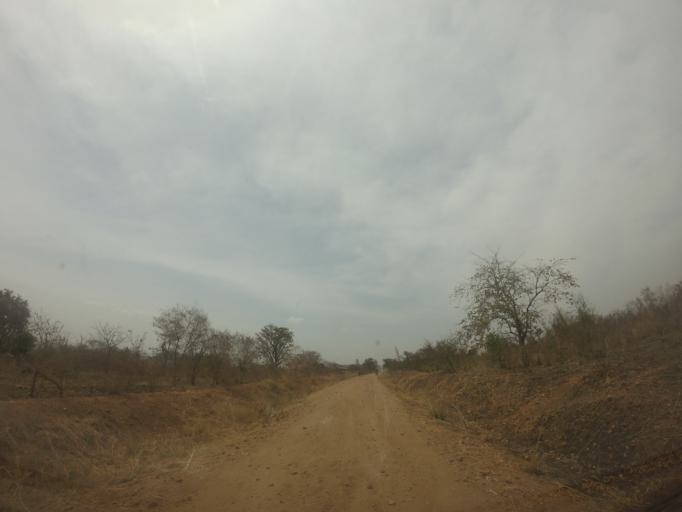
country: UG
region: Northern Region
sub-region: Nebbi District
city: Nebbi
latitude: 2.6343
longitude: 31.0312
